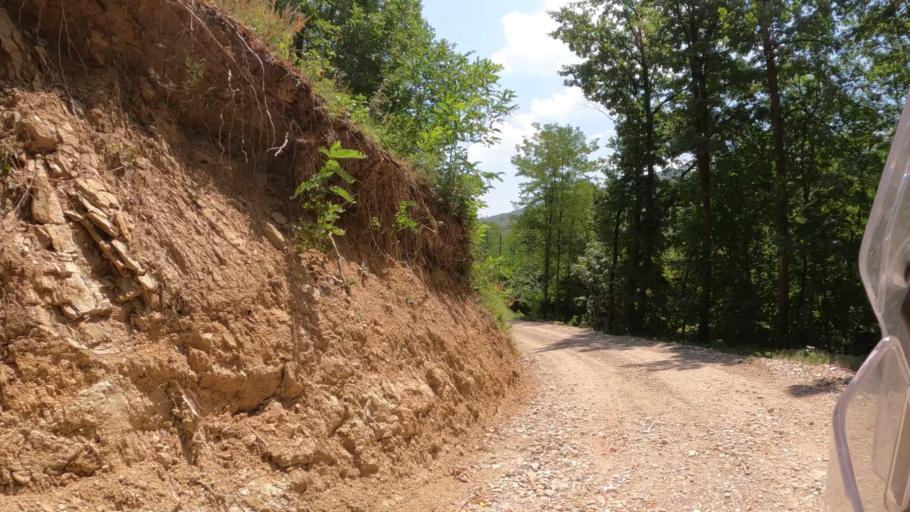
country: IT
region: Piedmont
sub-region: Provincia di Alessandria
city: Cassinelle-Concentrico
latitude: 44.5690
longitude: 8.5616
